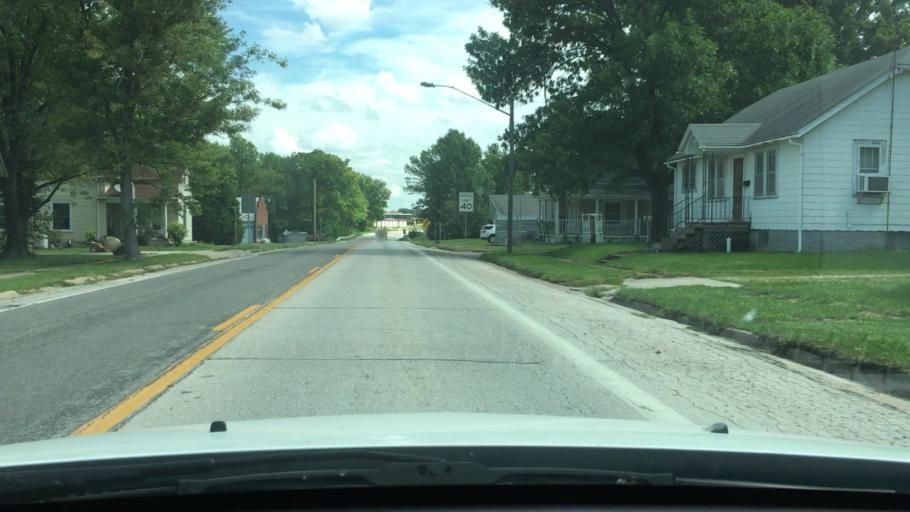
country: US
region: Missouri
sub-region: Audrain County
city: Vandalia
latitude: 39.3129
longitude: -91.4831
